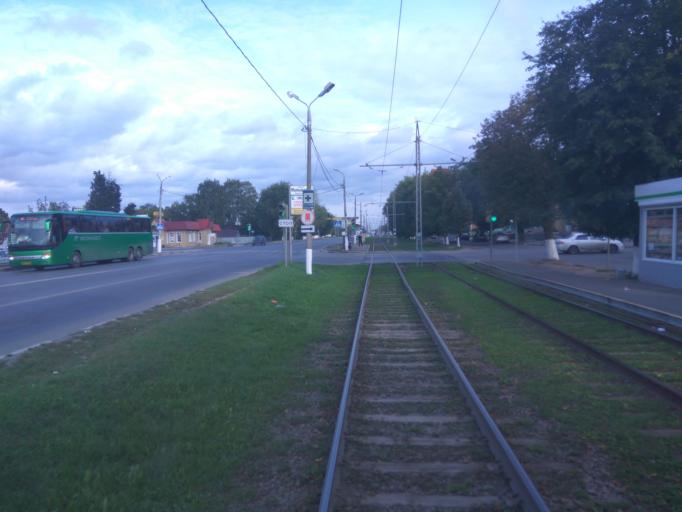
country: RU
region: Moskovskaya
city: Kolomna
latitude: 55.0864
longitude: 38.7947
